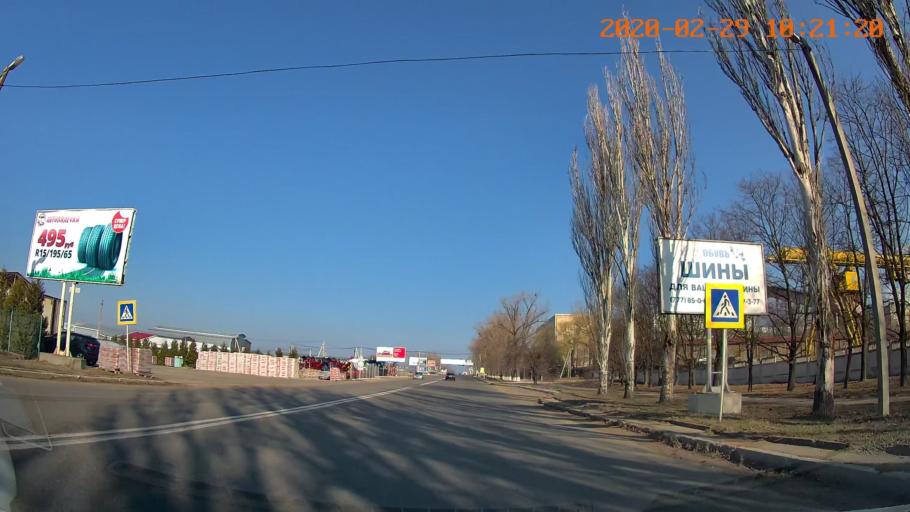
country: MD
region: Telenesti
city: Tiraspolul Nou
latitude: 46.8657
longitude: 29.6094
